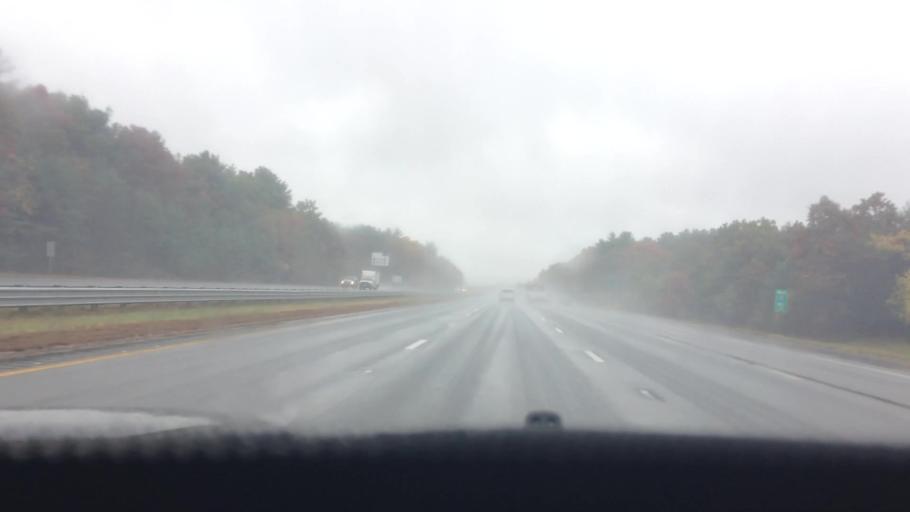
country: US
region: Massachusetts
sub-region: Middlesex County
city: Wilmington
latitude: 42.5627
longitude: -71.1430
